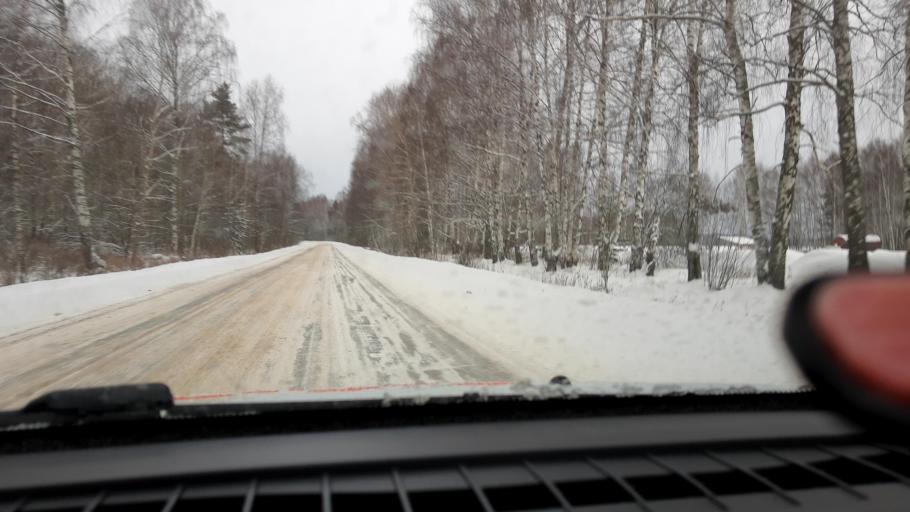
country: RU
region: Nizjnij Novgorod
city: Pamyat' Parizhskoy Kommuny
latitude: 56.2535
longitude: 44.4715
